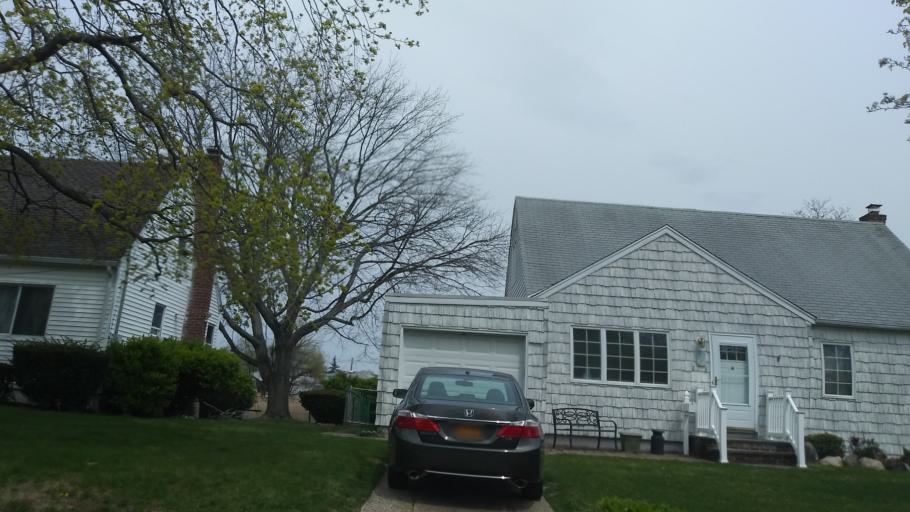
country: US
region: New York
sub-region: Nassau County
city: Baldwin Harbor
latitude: 40.6445
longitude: -73.6018
